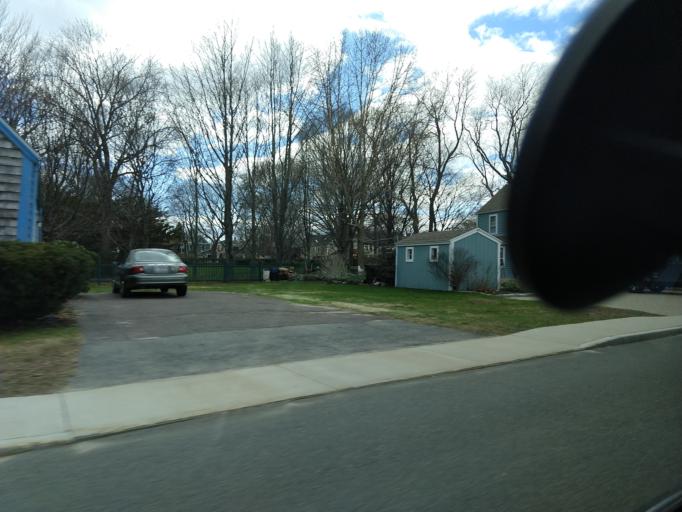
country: US
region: Massachusetts
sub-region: Essex County
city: Newburyport
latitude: 42.8055
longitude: -70.8566
